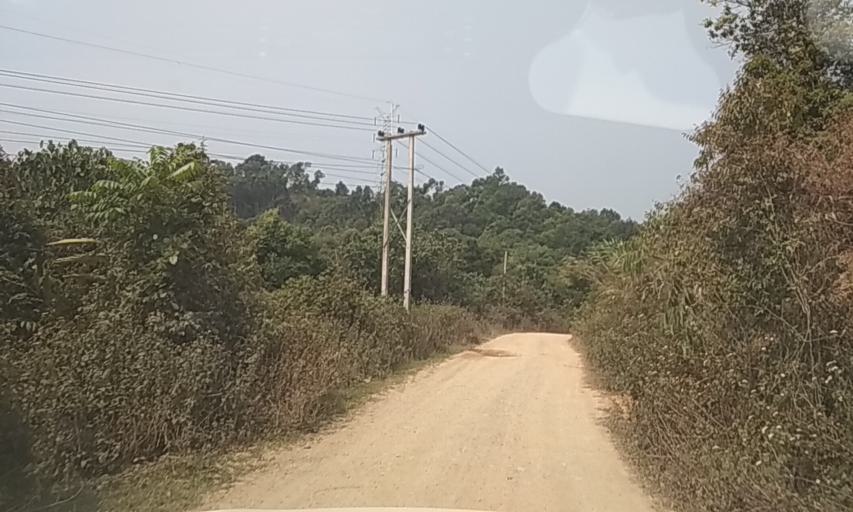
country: TH
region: Nan
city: Chaloem Phra Kiat
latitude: 20.0106
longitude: 101.1176
